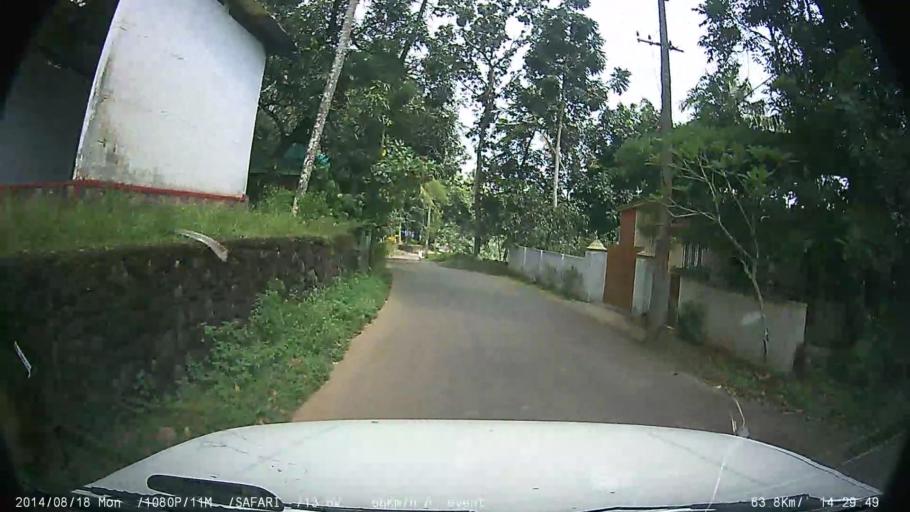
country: IN
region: Kerala
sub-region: Ernakulam
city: Piravam
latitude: 9.7919
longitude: 76.5479
